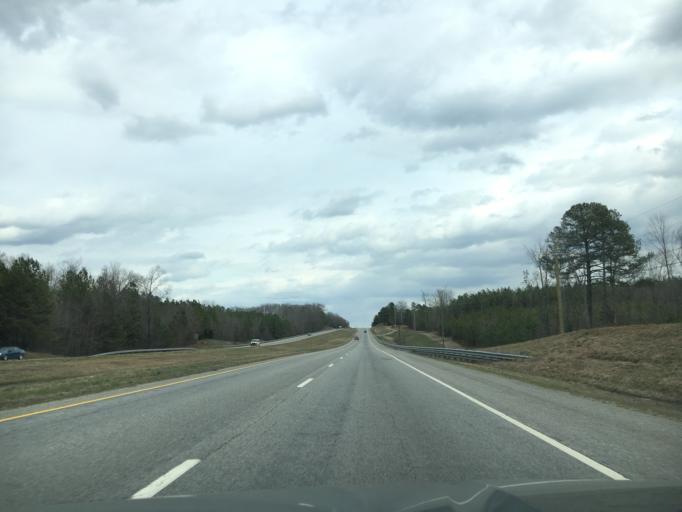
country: US
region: Virginia
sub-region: Mecklenburg County
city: Boydton
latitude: 36.6794
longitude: -78.3575
